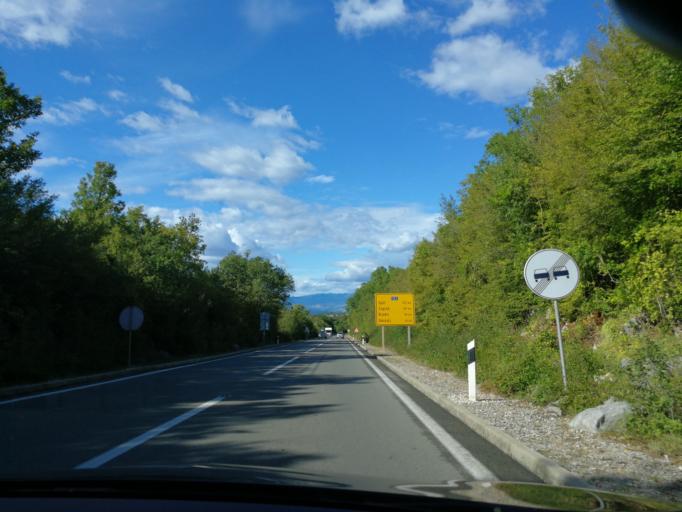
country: HR
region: Primorsko-Goranska
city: Njivice
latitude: 45.0963
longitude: 14.5367
